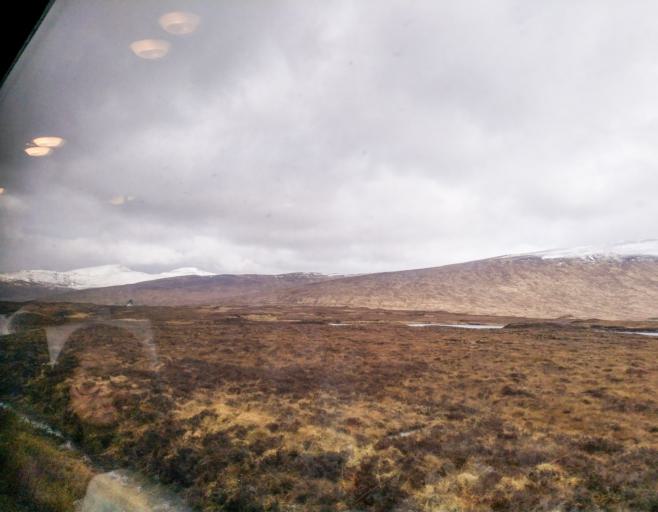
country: GB
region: Scotland
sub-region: Highland
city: Spean Bridge
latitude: 56.7523
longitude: -4.6792
